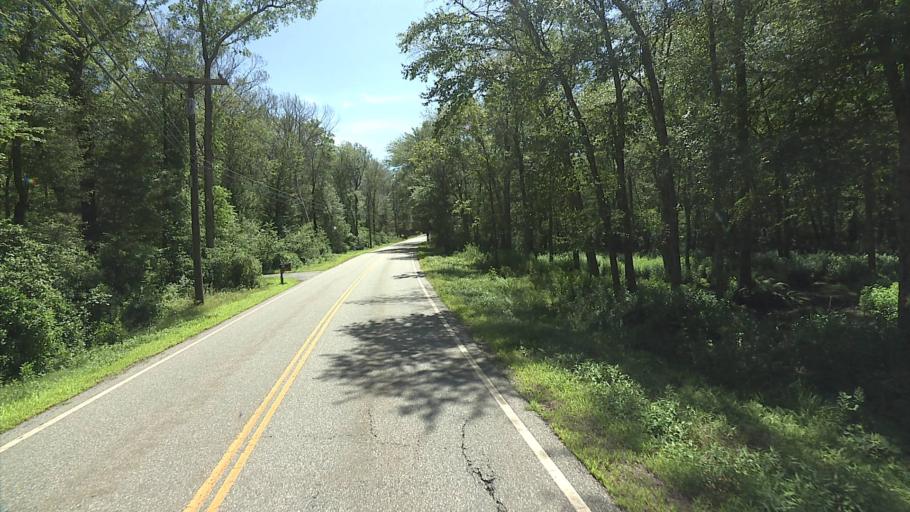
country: US
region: Connecticut
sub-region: Windham County
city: Windham
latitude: 41.7574
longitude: -72.0603
